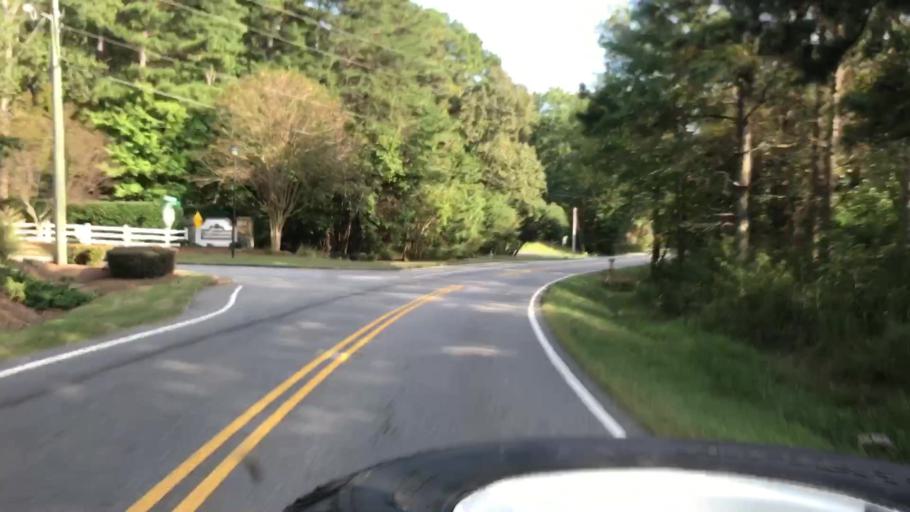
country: US
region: Georgia
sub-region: Forsyth County
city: Cumming
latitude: 34.1783
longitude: -84.0825
